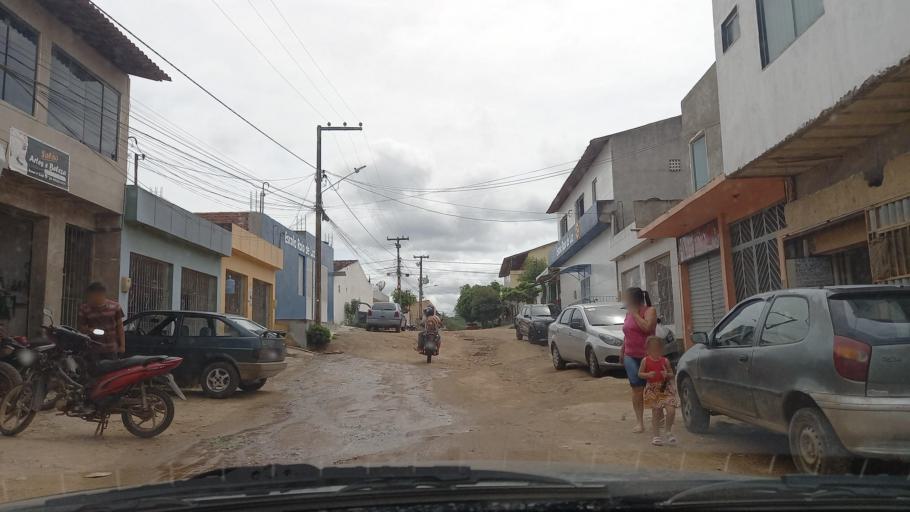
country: ET
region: Oromiya
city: Gore
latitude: 8.1945
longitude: 35.5800
